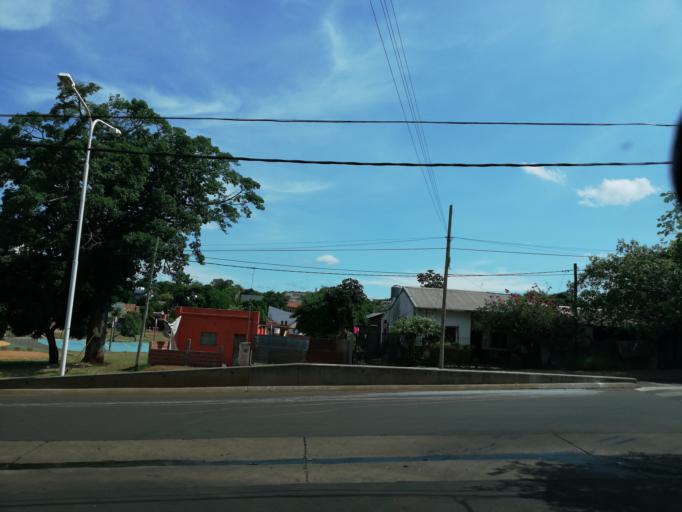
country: AR
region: Misiones
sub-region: Departamento de Capital
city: Posadas
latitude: -27.3785
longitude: -55.8896
